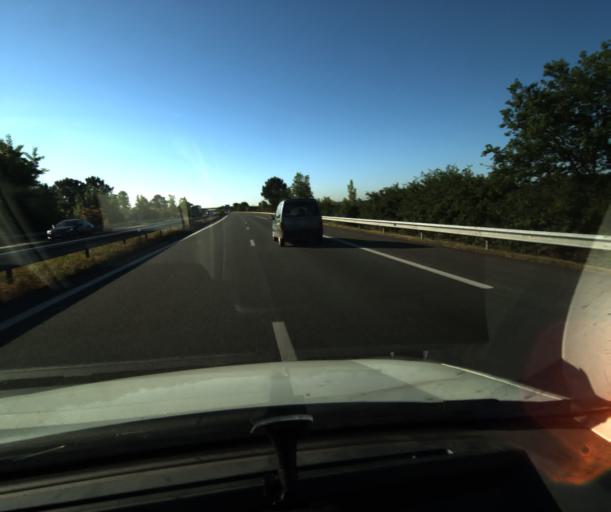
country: FR
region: Midi-Pyrenees
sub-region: Departement du Tarn-et-Garonne
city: Campsas
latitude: 43.9348
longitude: 1.3010
